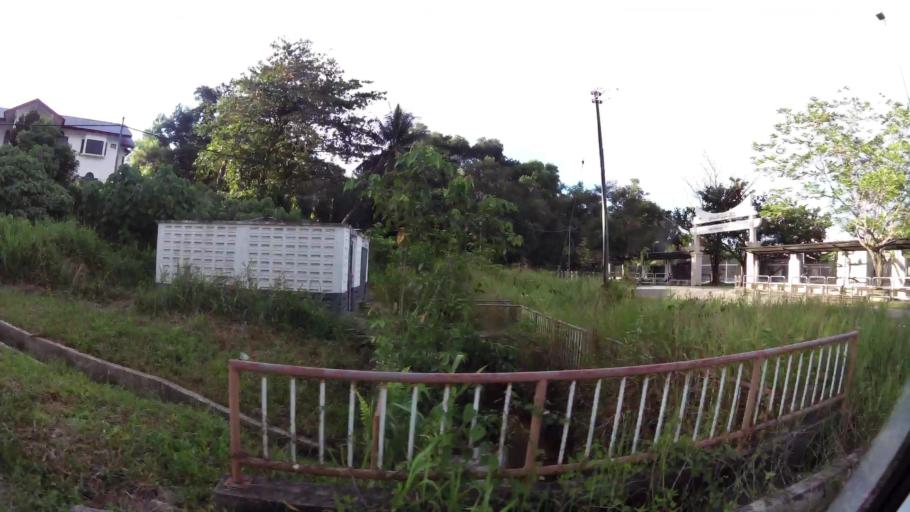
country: BN
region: Brunei and Muara
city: Bandar Seri Begawan
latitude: 4.9694
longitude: 114.9862
